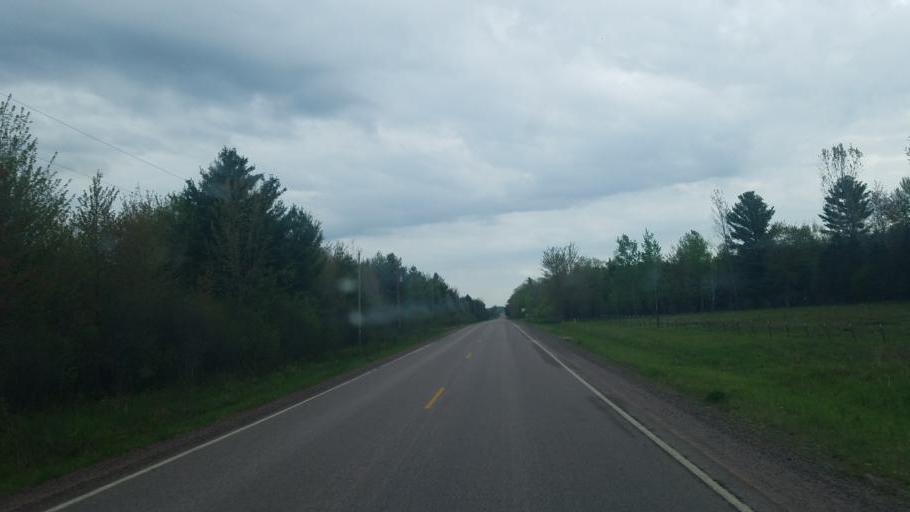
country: US
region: Wisconsin
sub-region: Wood County
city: Marshfield
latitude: 44.5598
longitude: -90.2999
